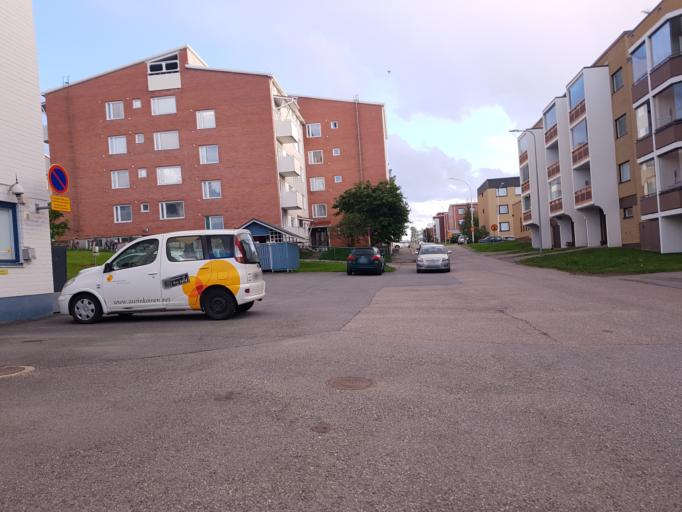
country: FI
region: Kainuu
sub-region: Kajaani
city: Kajaani
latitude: 64.2243
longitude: 27.7255
